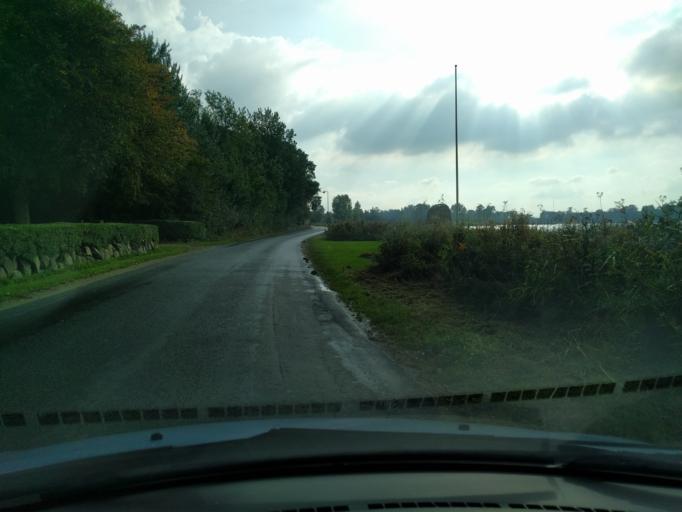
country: DK
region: South Denmark
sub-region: Kerteminde Kommune
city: Munkebo
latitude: 55.4275
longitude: 10.5835
